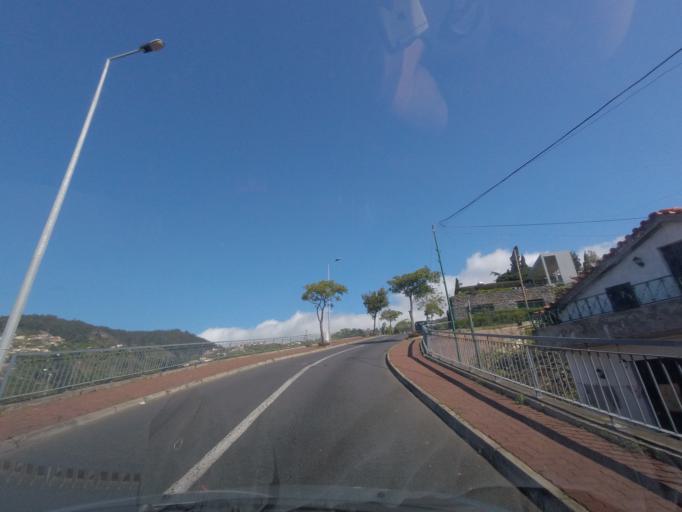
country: PT
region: Madeira
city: Camara de Lobos
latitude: 32.6691
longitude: -16.9798
